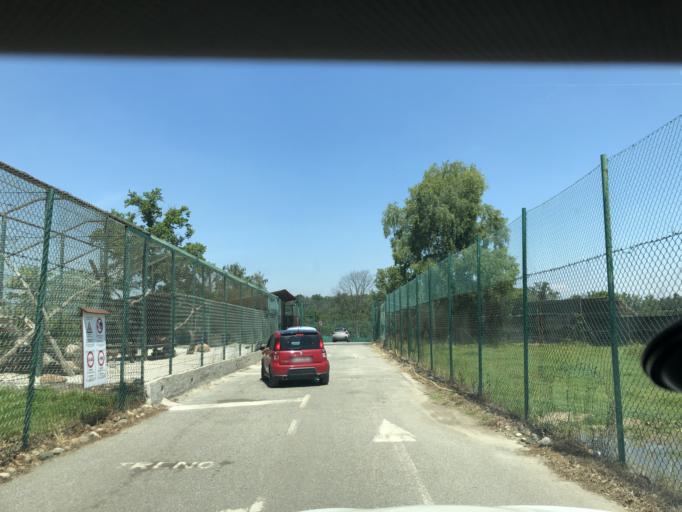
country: IT
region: Piedmont
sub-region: Provincia di Novara
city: Mezzomerico
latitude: 45.6385
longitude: 8.6128
